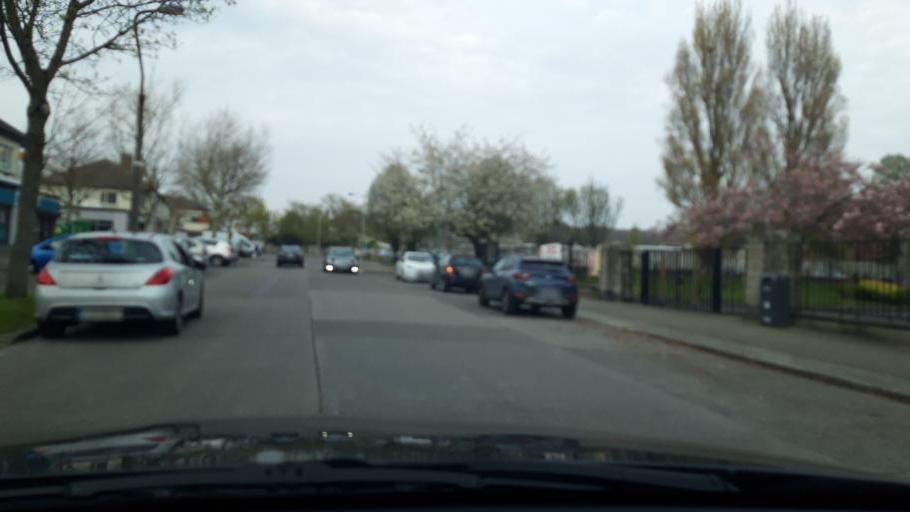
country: IE
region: Leinster
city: Dollymount
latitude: 53.3643
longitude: -6.1841
